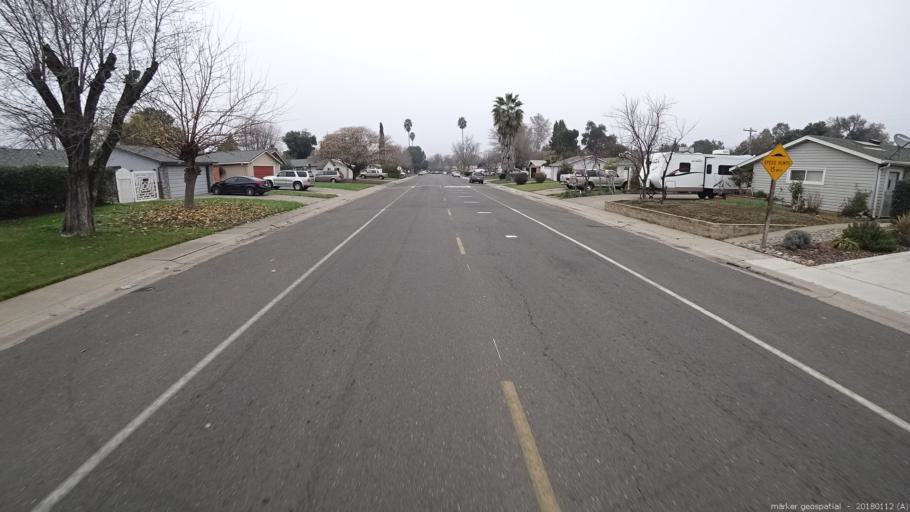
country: US
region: California
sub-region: Sacramento County
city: Rancho Cordova
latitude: 38.6102
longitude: -121.2813
